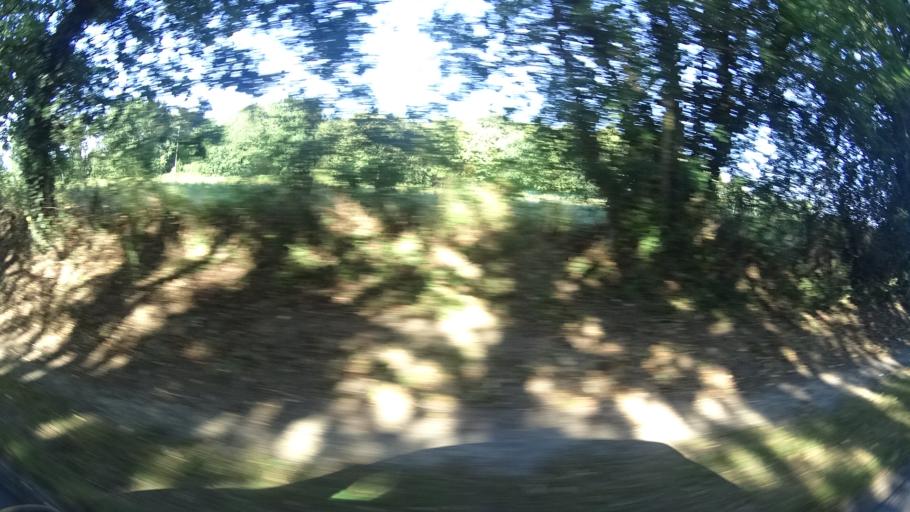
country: FR
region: Brittany
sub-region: Departement d'Ille-et-Vilaine
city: Langon
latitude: 47.7250
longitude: -1.8510
